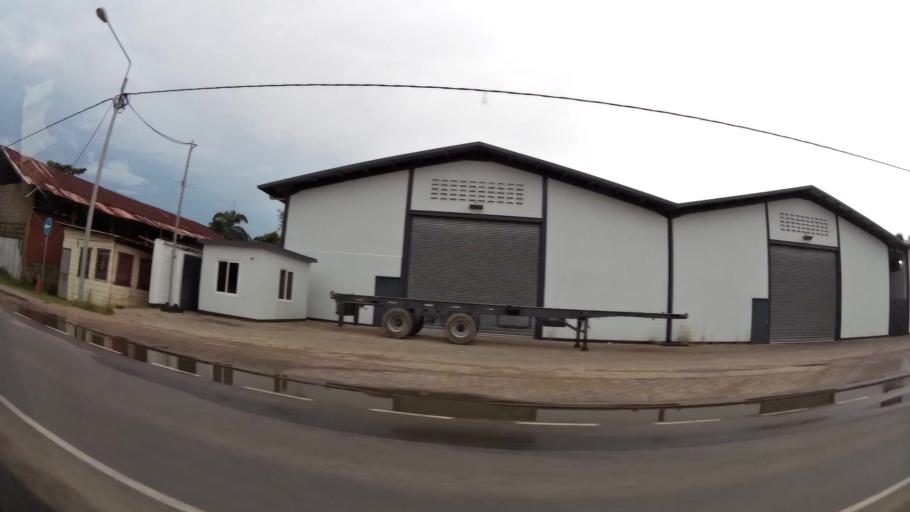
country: SR
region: Paramaribo
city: Paramaribo
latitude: 5.8025
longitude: -55.1832
